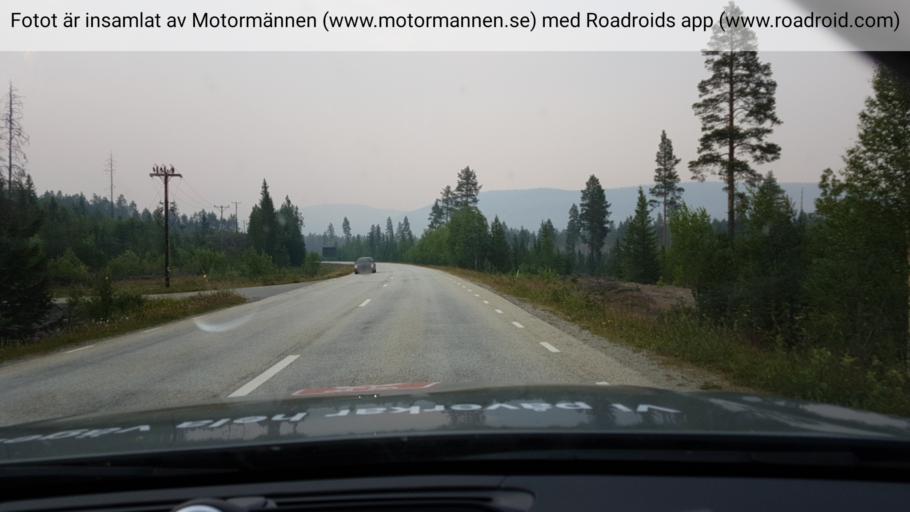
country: SE
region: Jaemtland
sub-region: Bergs Kommun
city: Hoverberg
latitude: 62.4816
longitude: 14.2307
